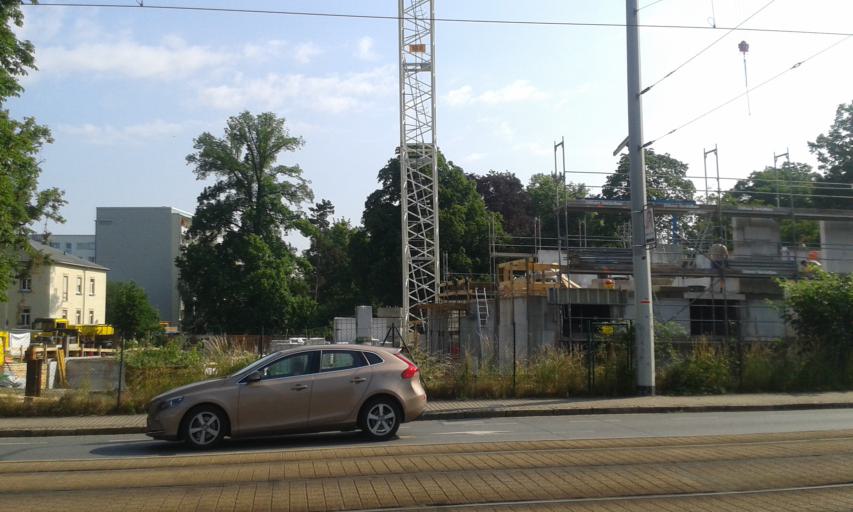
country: DE
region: Saxony
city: Dresden
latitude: 51.0310
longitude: 13.7857
